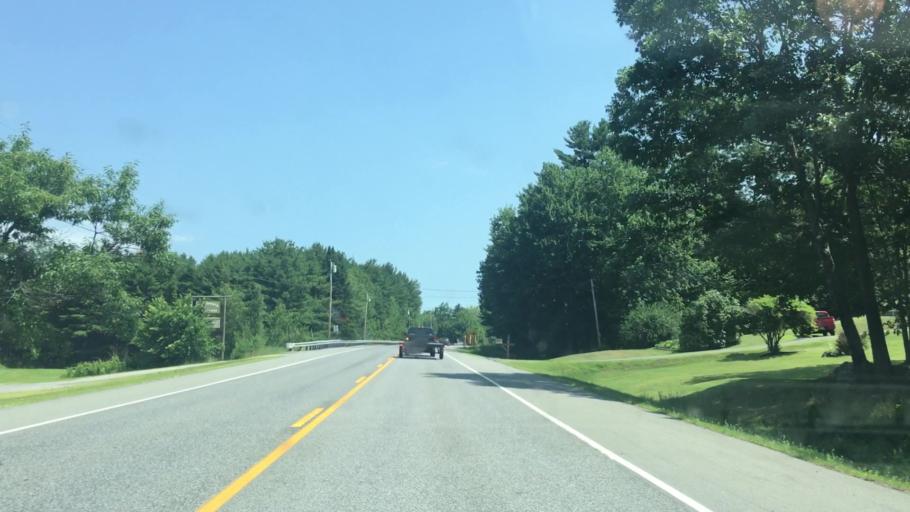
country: US
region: Maine
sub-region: Kennebec County
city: Monmouth
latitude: 44.2521
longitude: -70.0628
